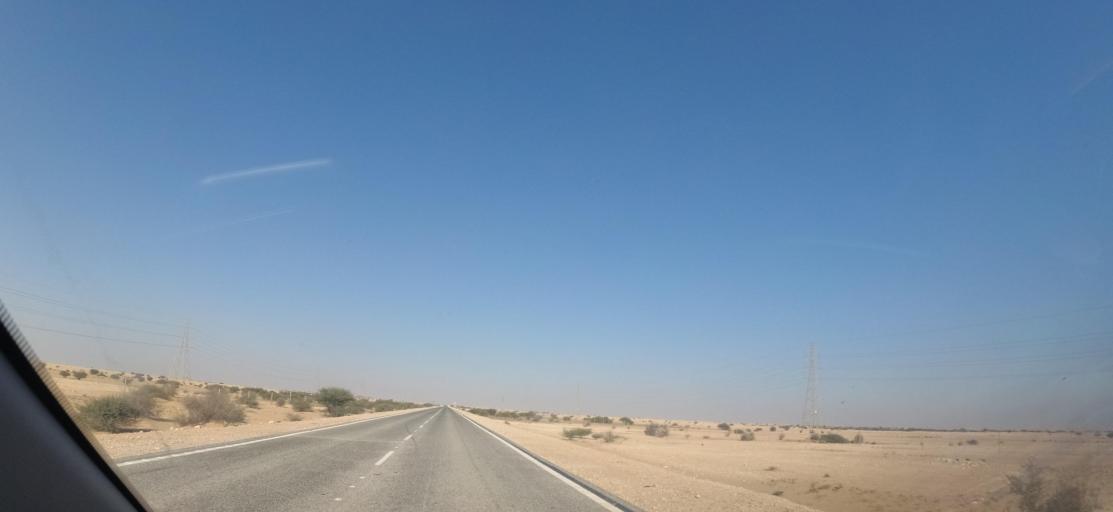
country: QA
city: Al Jumayliyah
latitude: 25.6412
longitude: 51.1040
